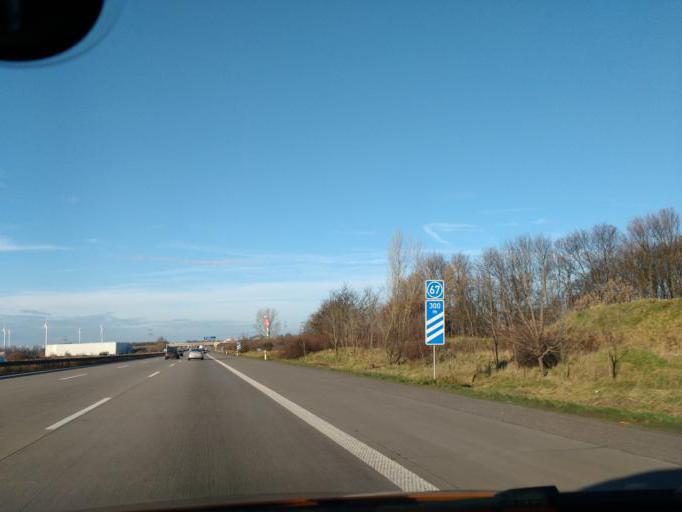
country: DE
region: Saxony-Anhalt
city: Hohenwarsleben
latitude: 52.1689
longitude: 11.4989
